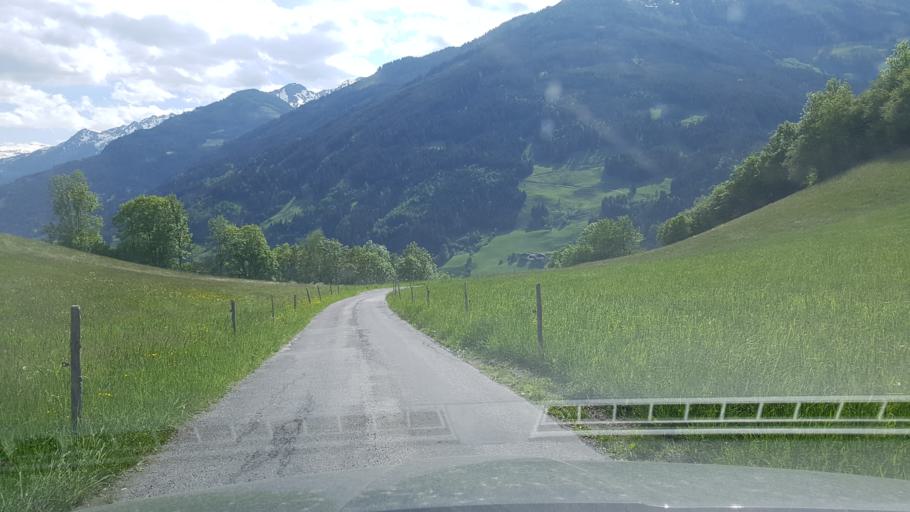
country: AT
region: Salzburg
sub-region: Politischer Bezirk Sankt Johann im Pongau
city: Dorfgastein
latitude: 47.2502
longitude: 13.1140
